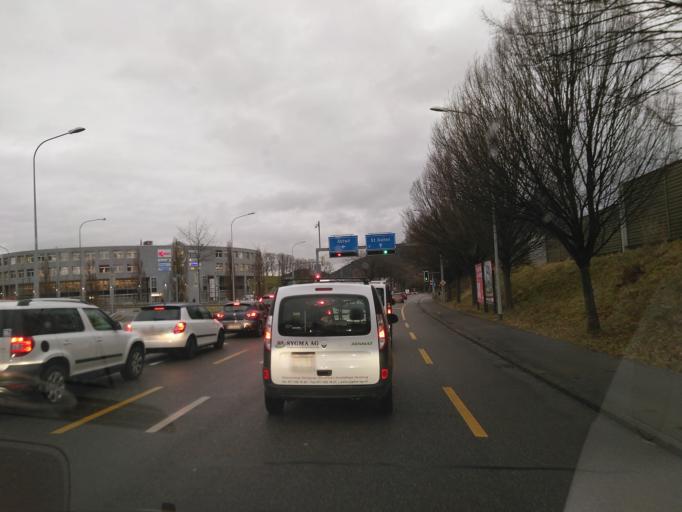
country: CH
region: Appenzell Ausserrhoden
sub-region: Bezirk Hinterland
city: Herisau
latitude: 47.4075
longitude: 9.3131
